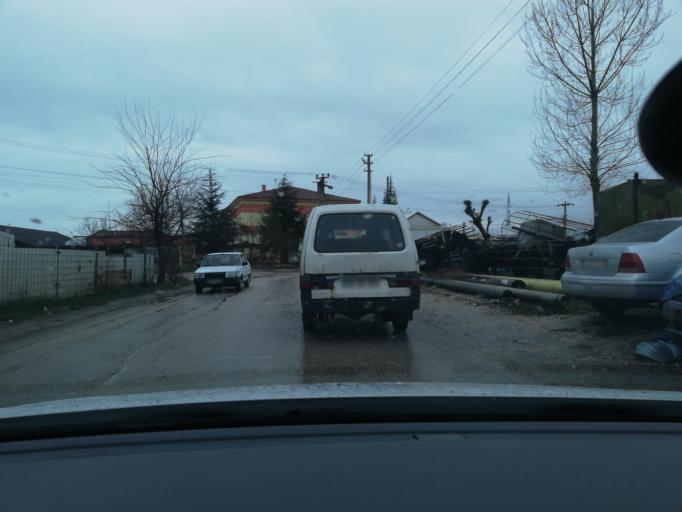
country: TR
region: Bolu
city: Bolu
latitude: 40.7376
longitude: 31.6303
